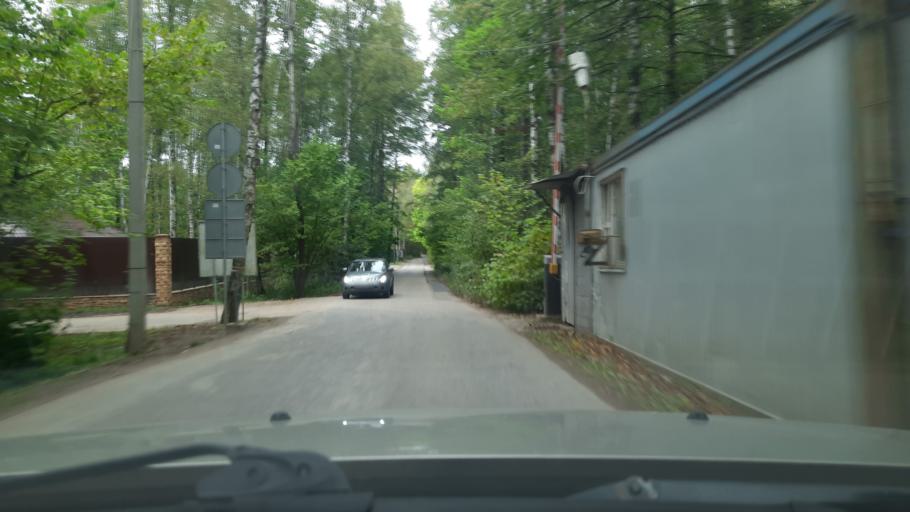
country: RU
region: Moskovskaya
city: Barvikha
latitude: 55.7131
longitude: 37.3073
